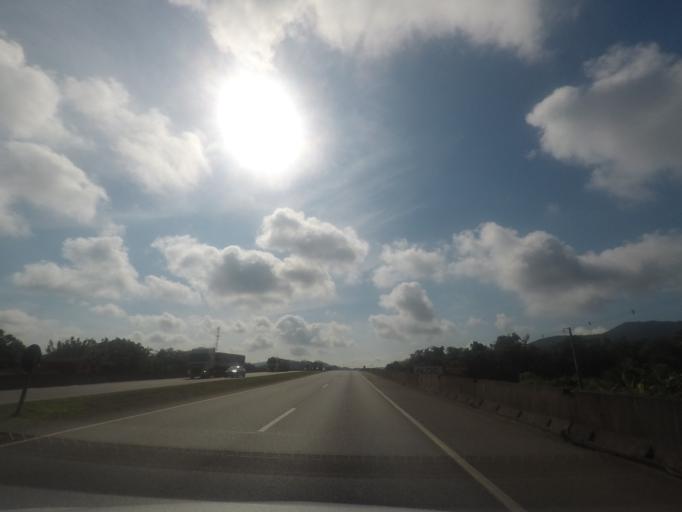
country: BR
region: Parana
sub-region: Antonina
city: Antonina
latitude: -25.5490
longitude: -48.7935
